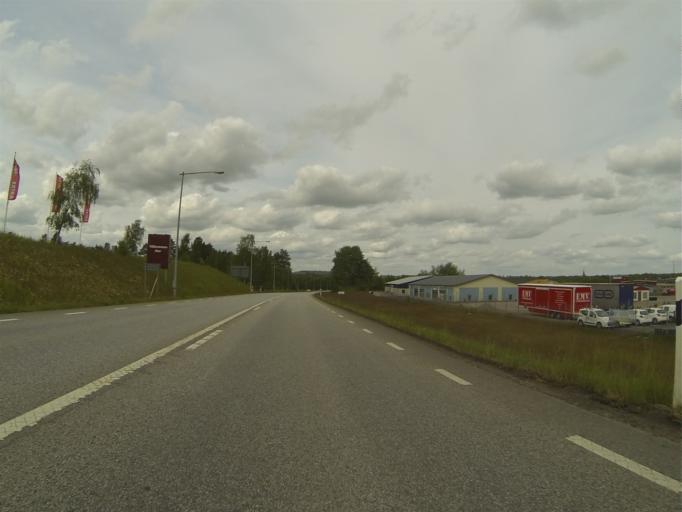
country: SE
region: Skane
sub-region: Sjobo Kommun
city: Sjoebo
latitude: 55.6363
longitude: 13.6822
